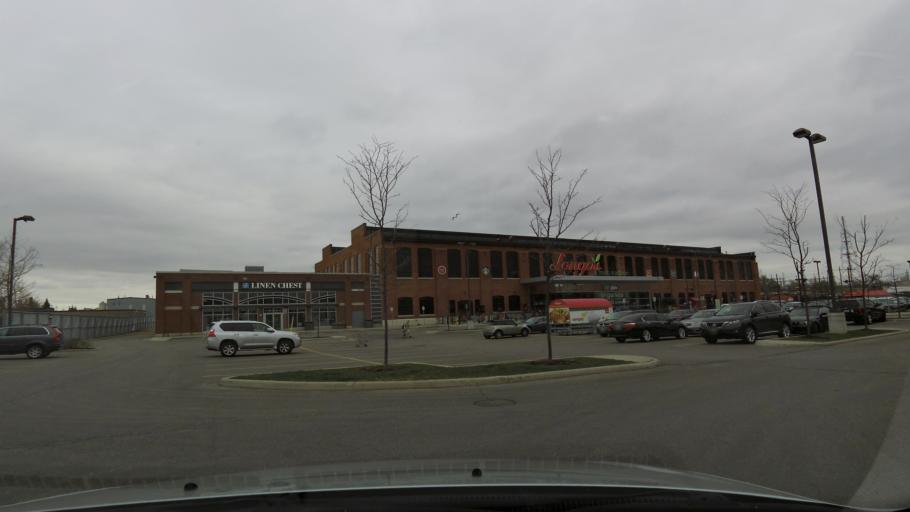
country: CA
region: Ontario
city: Toronto
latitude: 43.7069
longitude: -79.3607
